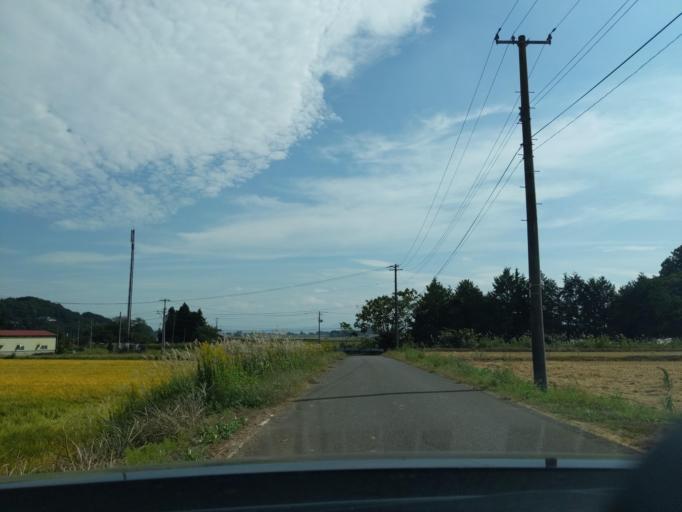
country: JP
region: Fukushima
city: Koriyama
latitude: 37.3689
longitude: 140.2708
